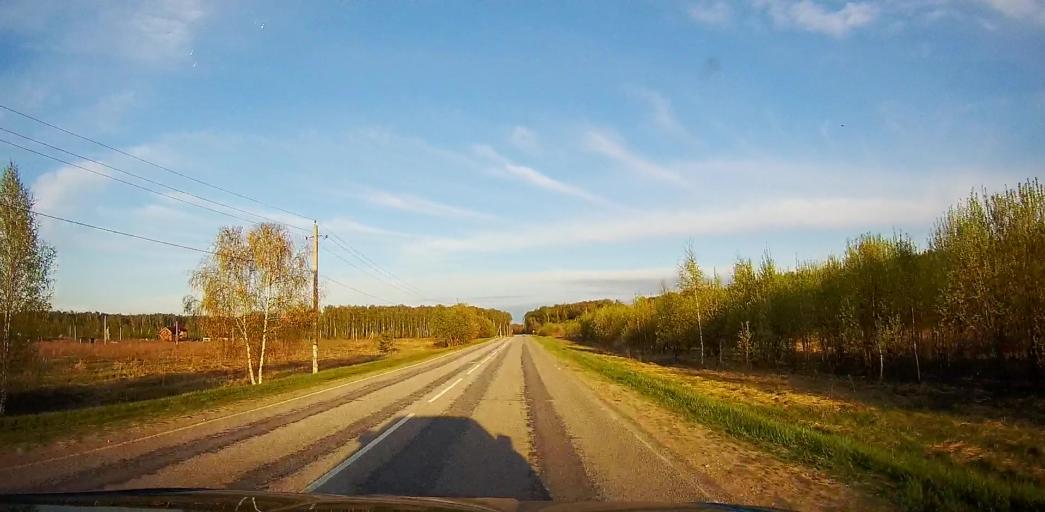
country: RU
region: Moskovskaya
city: Meshcherino
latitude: 55.2301
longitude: 38.3773
